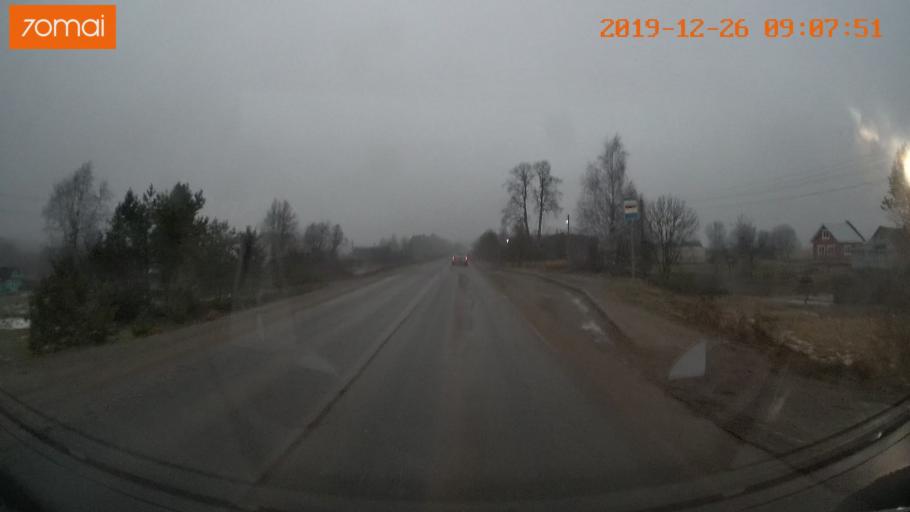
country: RU
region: Vologda
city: Gryazovets
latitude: 58.8505
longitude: 40.2469
